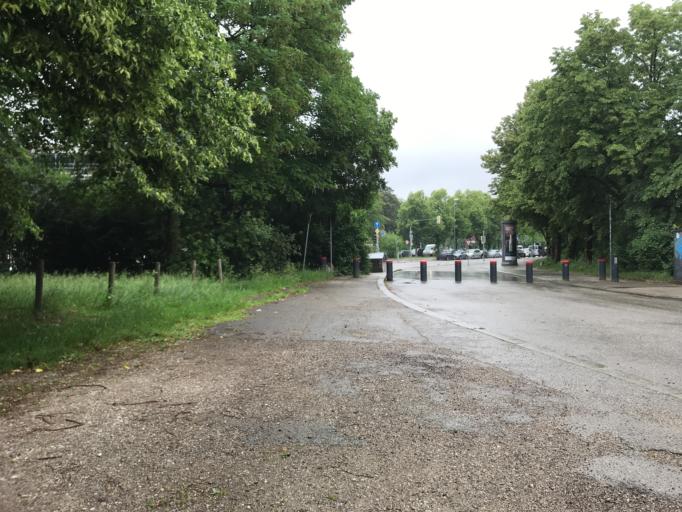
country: DE
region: Bavaria
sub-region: Upper Bavaria
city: Munich
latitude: 48.1314
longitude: 11.5460
